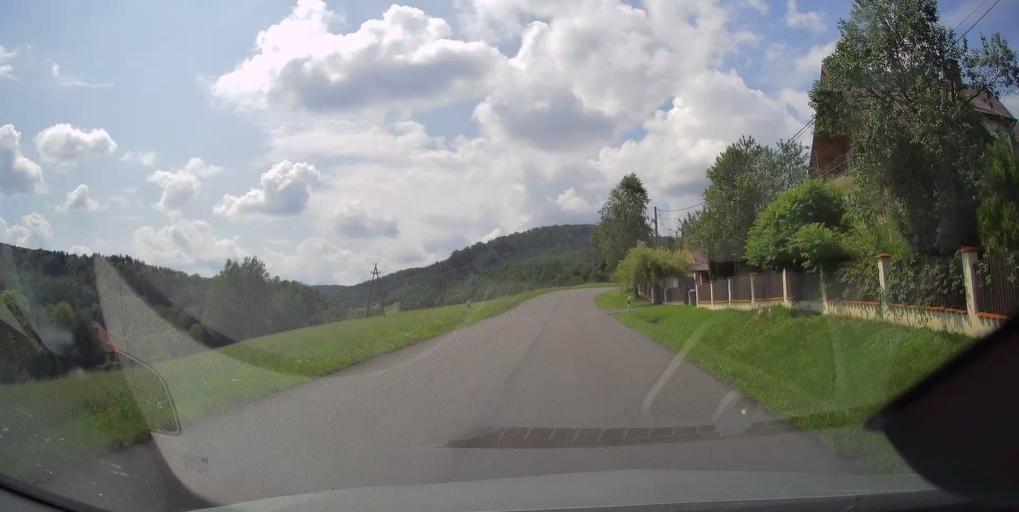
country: PL
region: Lesser Poland Voivodeship
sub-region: Powiat tarnowski
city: Zakliczyn
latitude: 49.7893
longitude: 20.7951
